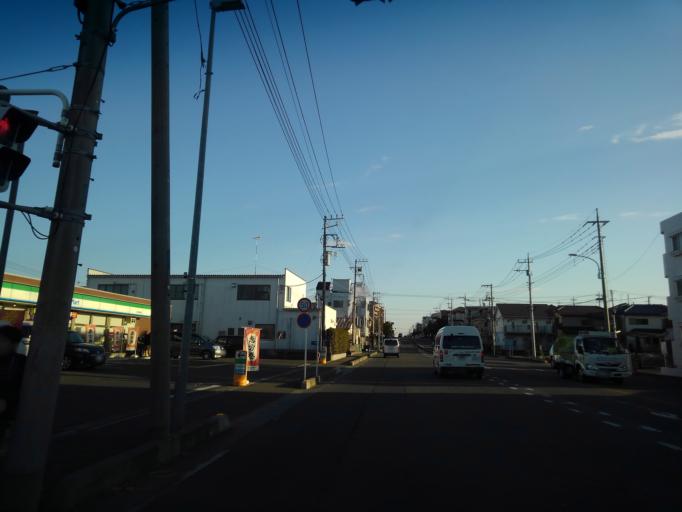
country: JP
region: Saitama
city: Tokorozawa
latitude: 35.7959
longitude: 139.5032
